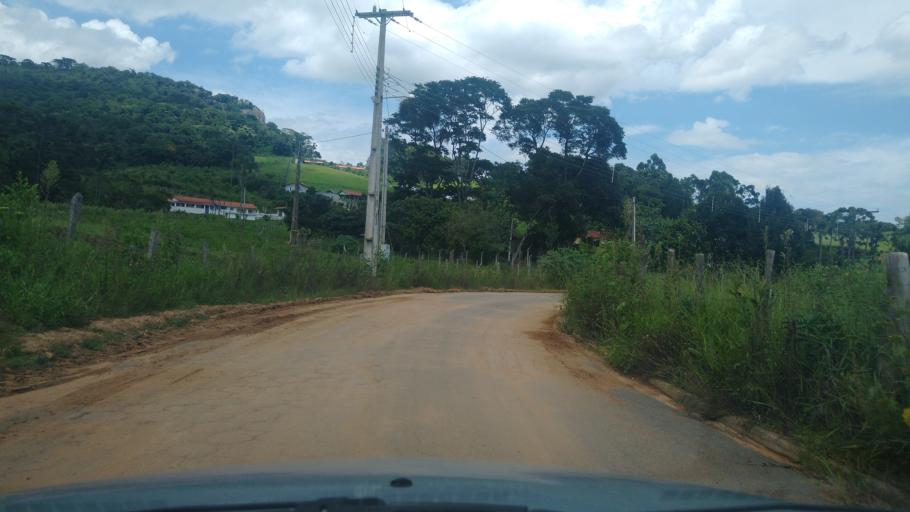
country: BR
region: Minas Gerais
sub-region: Extrema
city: Extrema
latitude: -22.7288
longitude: -46.3166
